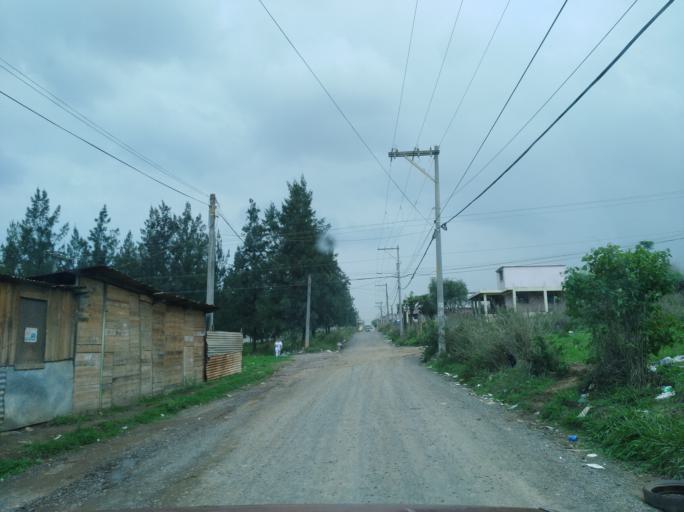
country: GT
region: Guatemala
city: Villa Nueva
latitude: 14.5280
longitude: -90.6218
